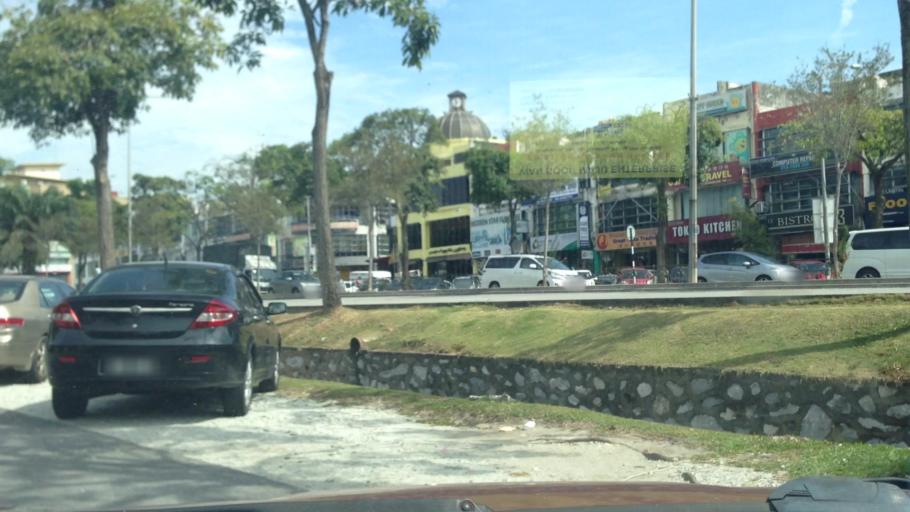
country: MY
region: Selangor
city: Subang Jaya
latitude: 3.0467
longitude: 101.5853
